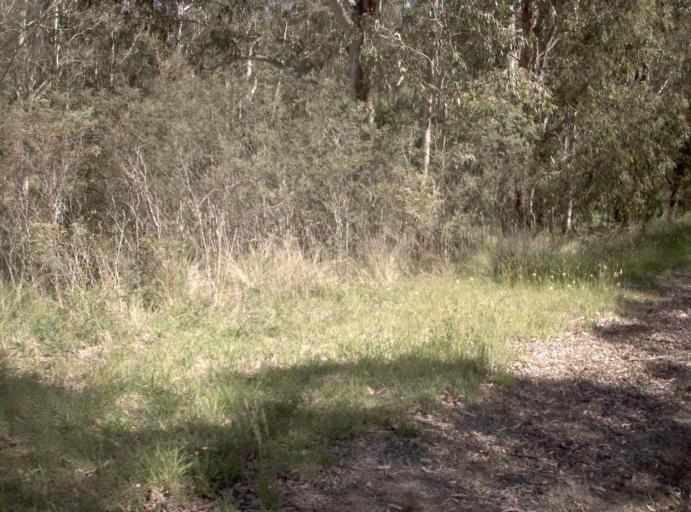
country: AU
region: New South Wales
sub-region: Bombala
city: Bombala
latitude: -37.1560
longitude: 148.7246
